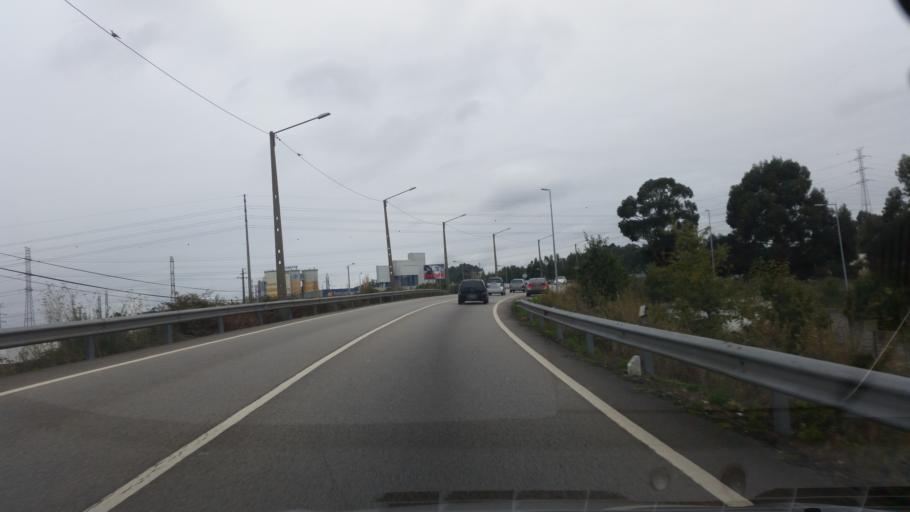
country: PT
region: Porto
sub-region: Valongo
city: Ermesinde
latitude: 41.2314
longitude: -8.5541
